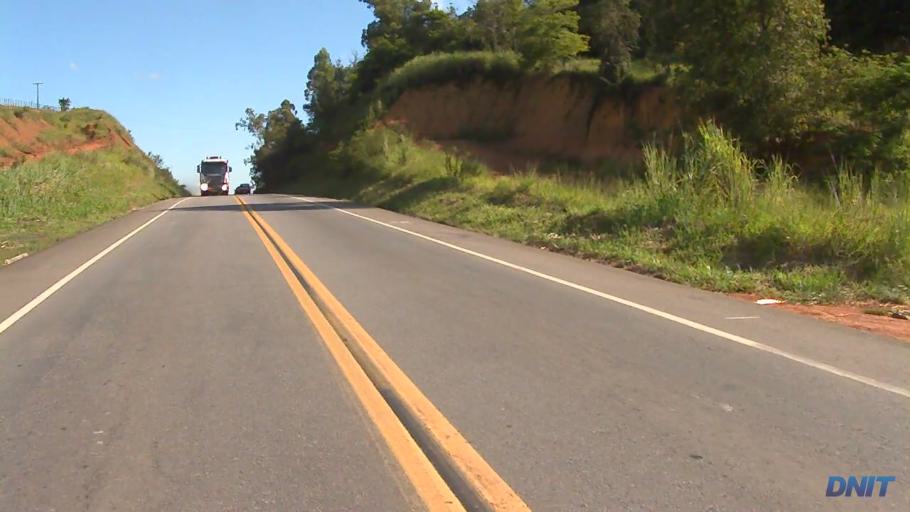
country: BR
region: Minas Gerais
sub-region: Belo Oriente
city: Belo Oriente
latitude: -19.2474
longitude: -42.3381
